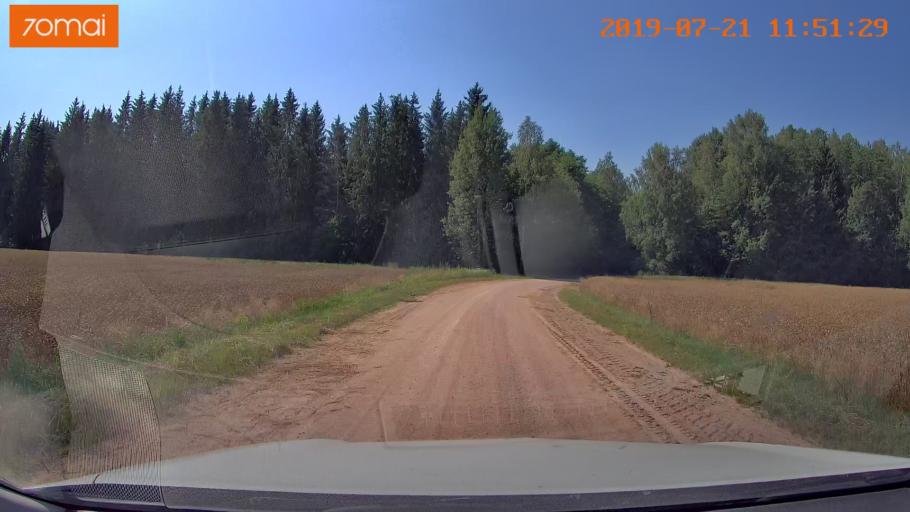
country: BY
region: Grodnenskaya
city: Lyubcha
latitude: 53.8830
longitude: 26.0124
